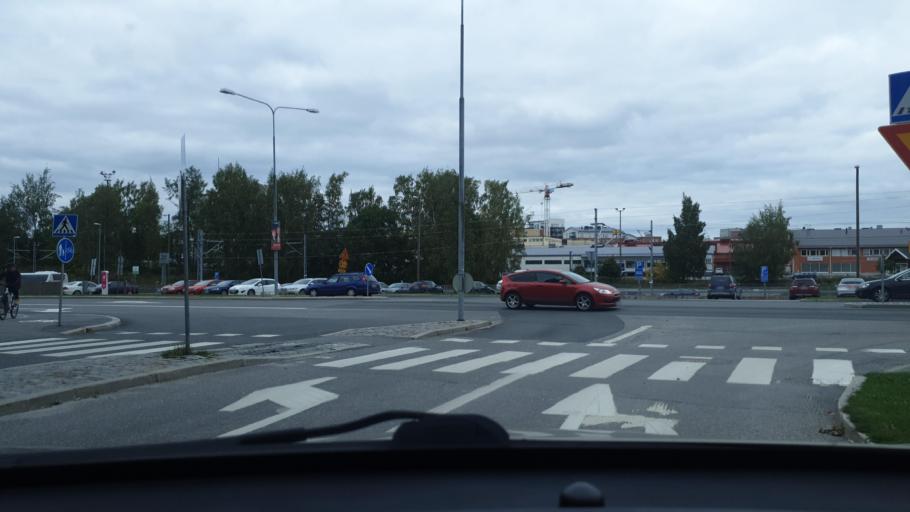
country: FI
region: Ostrobothnia
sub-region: Vaasa
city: Vaasa
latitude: 63.0956
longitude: 21.6260
